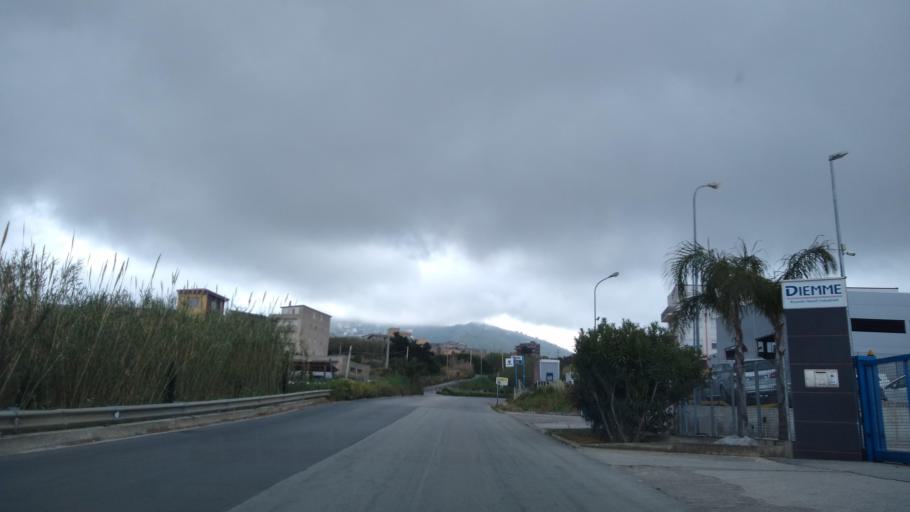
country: IT
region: Sicily
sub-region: Trapani
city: Alcamo
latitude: 37.9884
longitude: 12.9529
